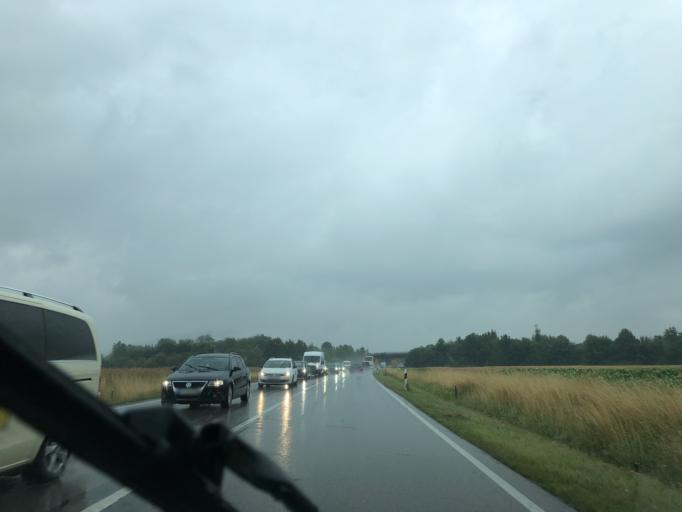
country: DE
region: Bavaria
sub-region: Upper Bavaria
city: Erding
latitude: 48.3227
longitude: 11.8825
